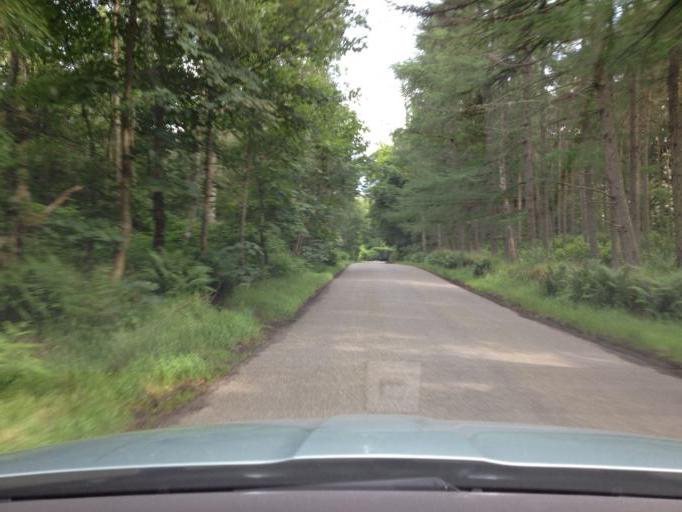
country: GB
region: Scotland
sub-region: Angus
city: Brechin
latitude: 56.8364
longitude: -2.6559
